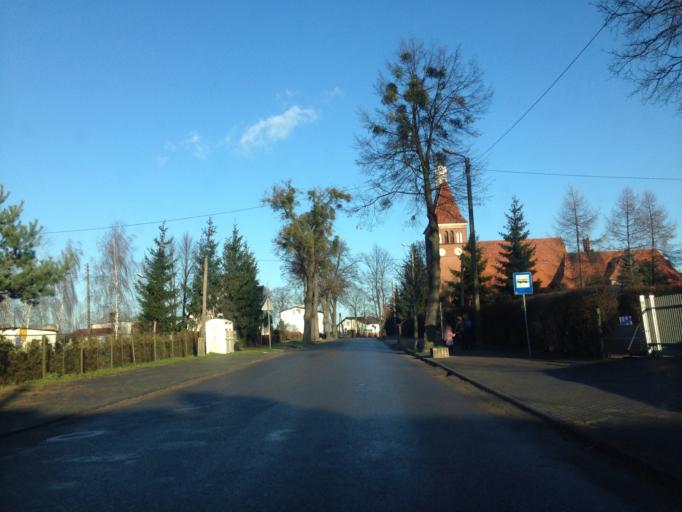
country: PL
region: Kujawsko-Pomorskie
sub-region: Powiat brodnicki
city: Jablonowo Pomorskie
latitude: 53.3936
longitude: 19.1562
